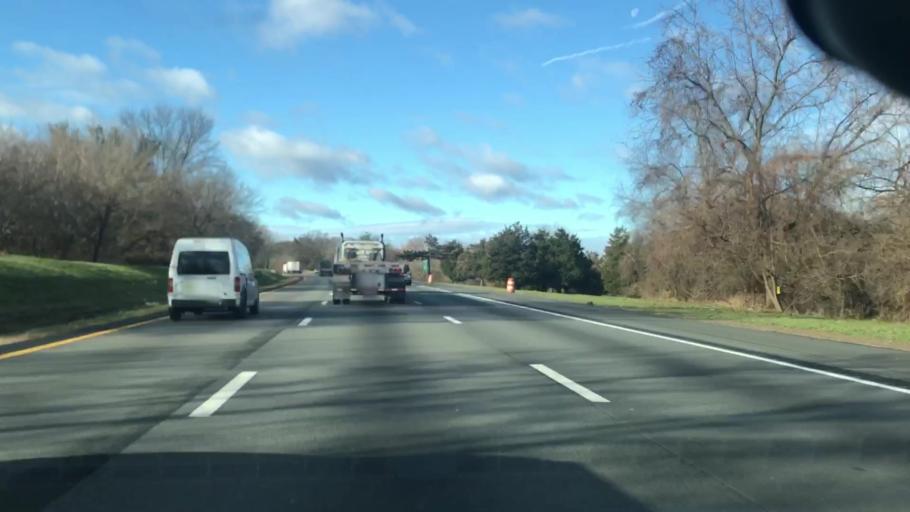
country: US
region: New Jersey
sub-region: Hunterdon County
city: Whitehouse Station
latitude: 40.6521
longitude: -74.7841
